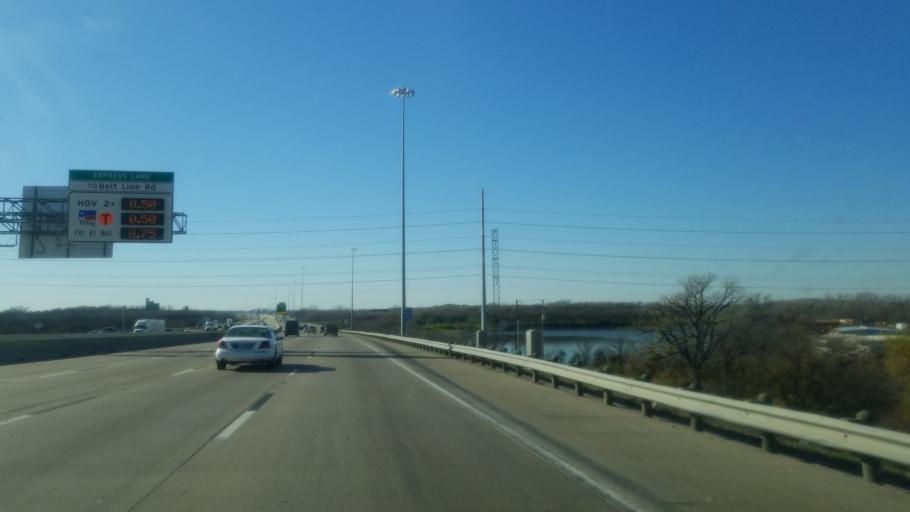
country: US
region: Texas
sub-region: Dallas County
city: Cockrell Hill
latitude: 32.7664
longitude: -96.9176
